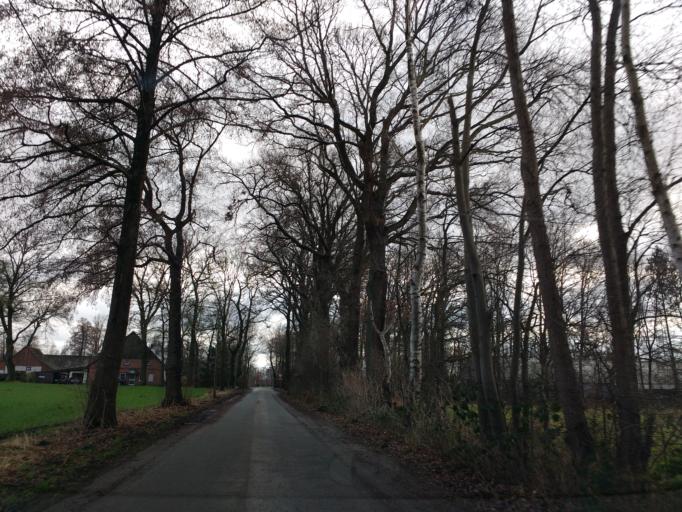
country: DE
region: North Rhine-Westphalia
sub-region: Regierungsbezirk Detmold
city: Hovelhof
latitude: 51.8227
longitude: 8.6915
